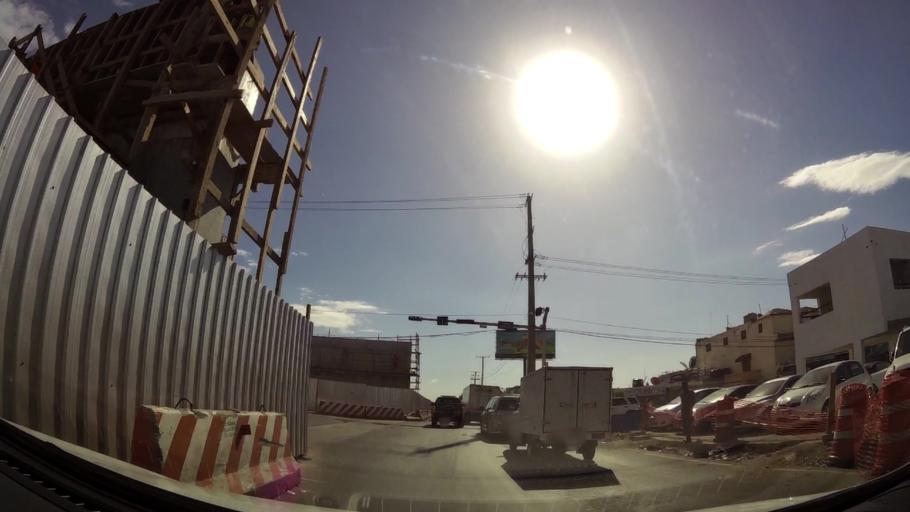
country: DO
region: Santo Domingo
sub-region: Santo Domingo
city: Boca Chica
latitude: 18.4548
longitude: -69.6060
